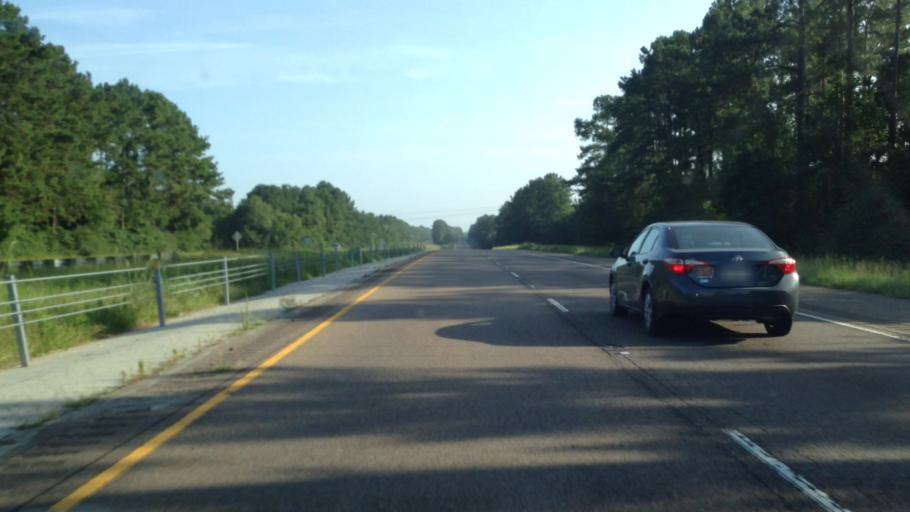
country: US
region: Louisiana
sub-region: Tangipahoa Parish
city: Roseland
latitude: 30.7817
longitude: -90.5329
